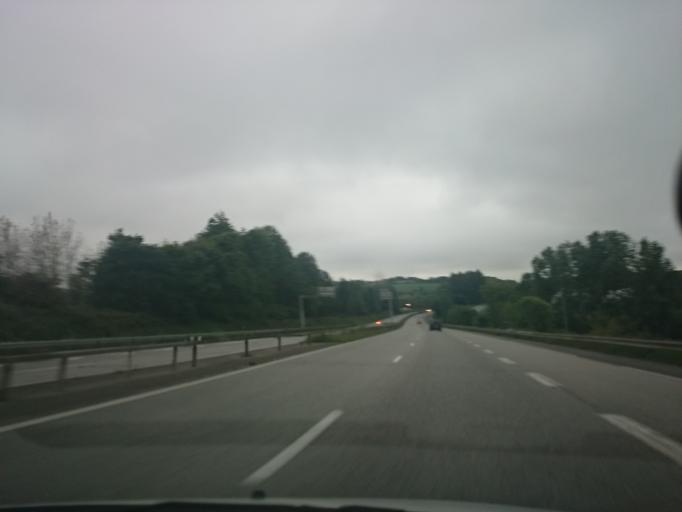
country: FR
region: Brittany
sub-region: Departement du Finistere
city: Ergue-Gaberic
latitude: 48.0024
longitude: -4.0542
